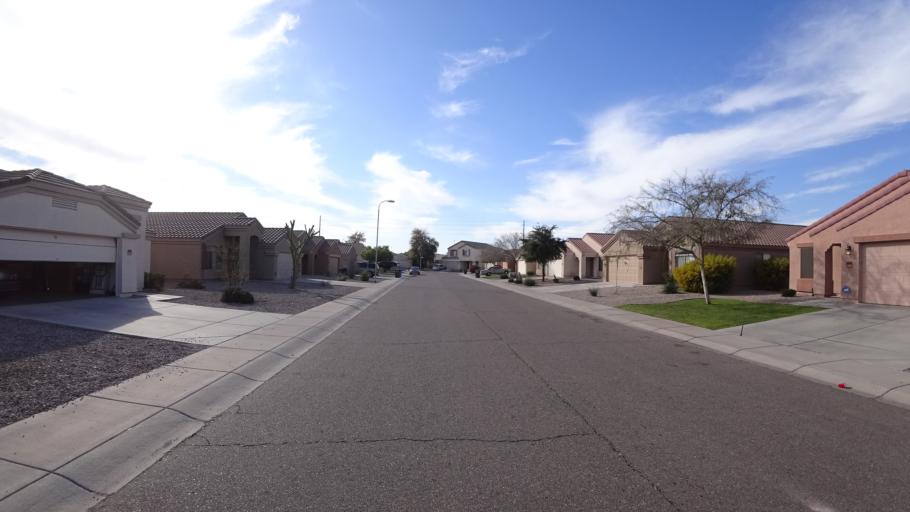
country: US
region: Arizona
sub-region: Maricopa County
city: Tolleson
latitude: 33.4277
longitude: -112.2881
